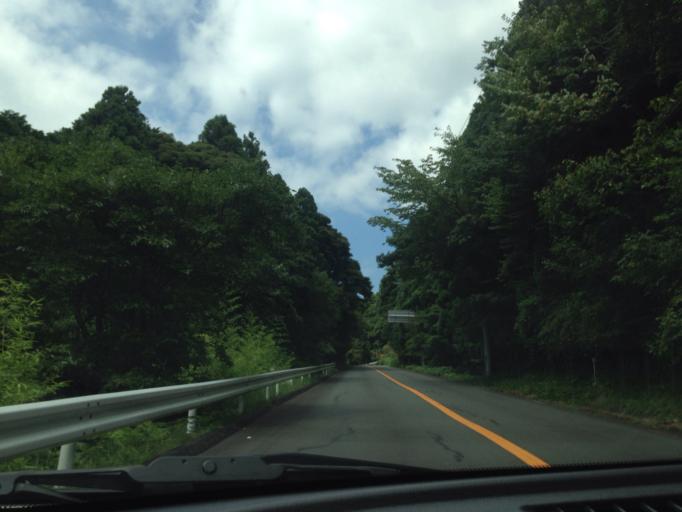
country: JP
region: Shizuoka
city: Shimoda
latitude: 34.7052
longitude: 138.7587
